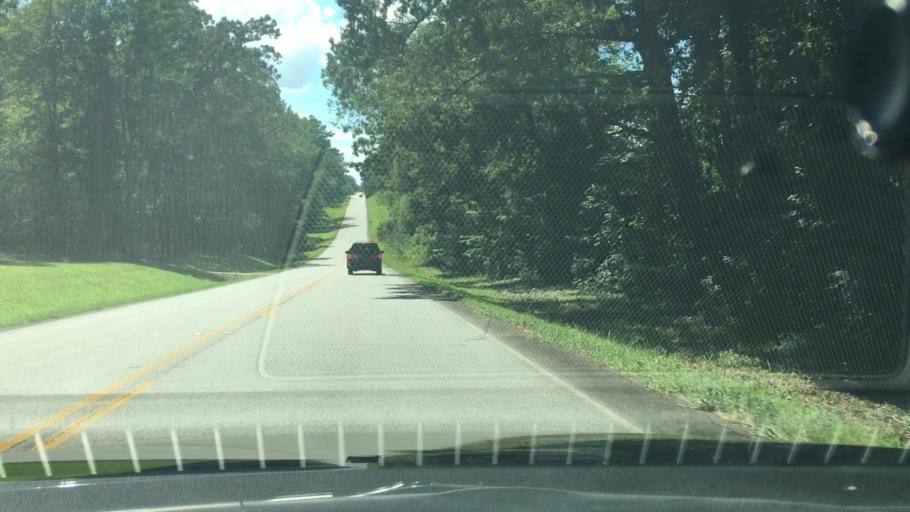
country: US
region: Georgia
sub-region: Jasper County
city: Monticello
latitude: 33.3051
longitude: -83.5879
